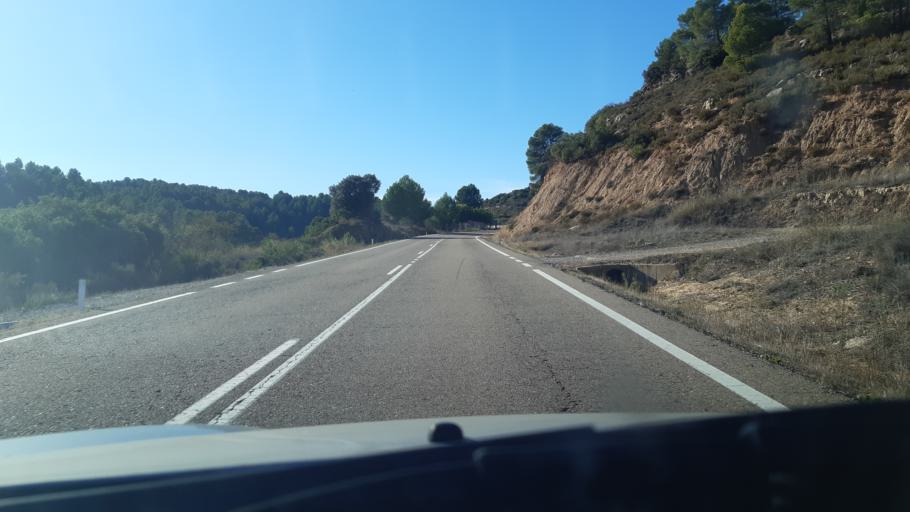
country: ES
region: Aragon
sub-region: Provincia de Teruel
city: Valjunquera
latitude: 40.9494
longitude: 0.0376
